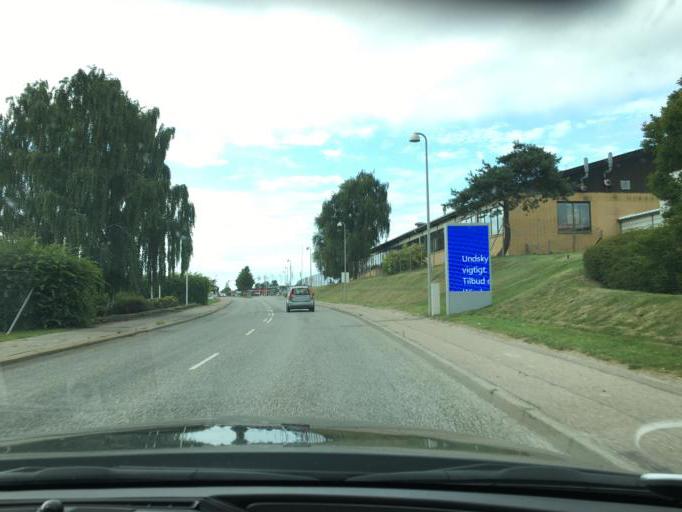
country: DK
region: Capital Region
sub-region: Gribskov Kommune
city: Helsinge
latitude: 56.0139
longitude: 12.1999
